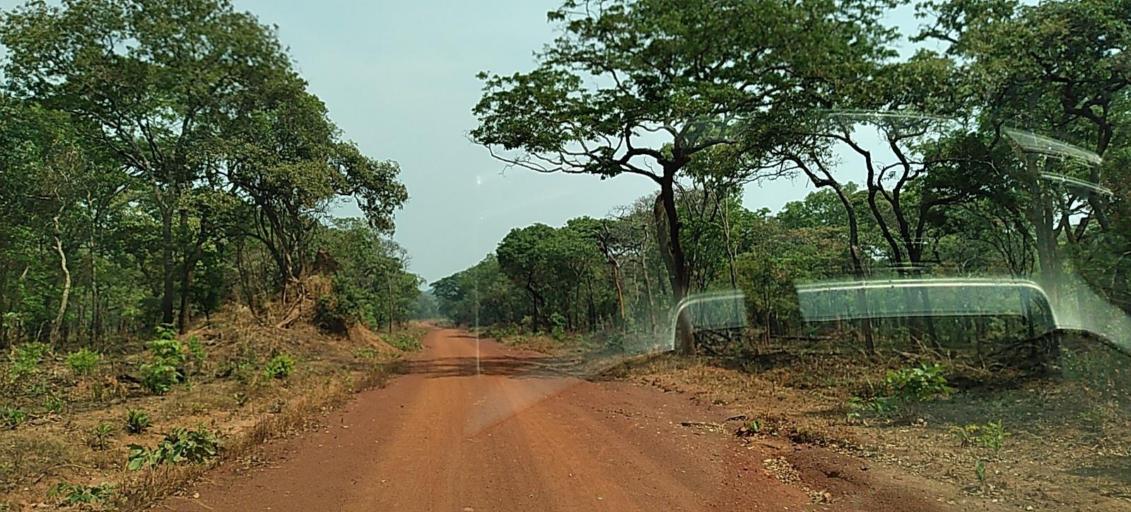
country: ZM
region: North-Western
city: Kansanshi
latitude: -12.0038
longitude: 26.8426
